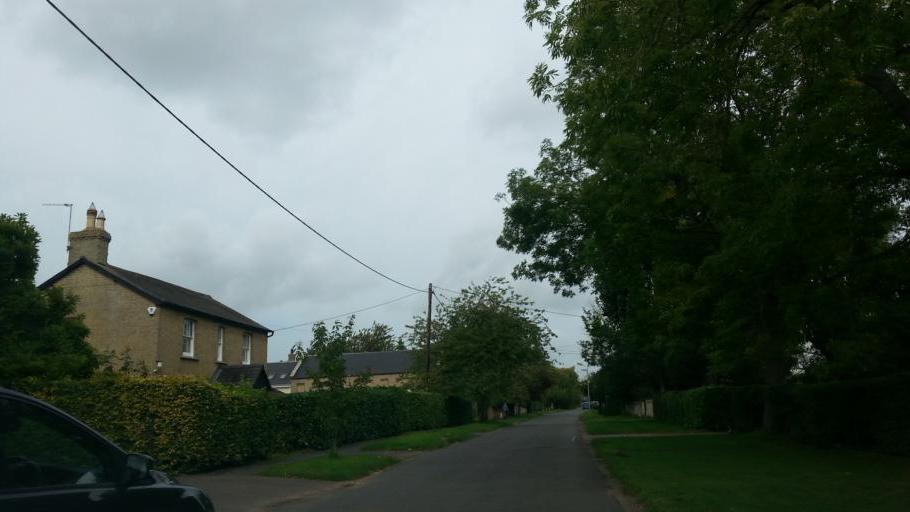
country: GB
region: England
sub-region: Cambridgeshire
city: Comberton
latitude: 52.1886
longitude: 0.0186
